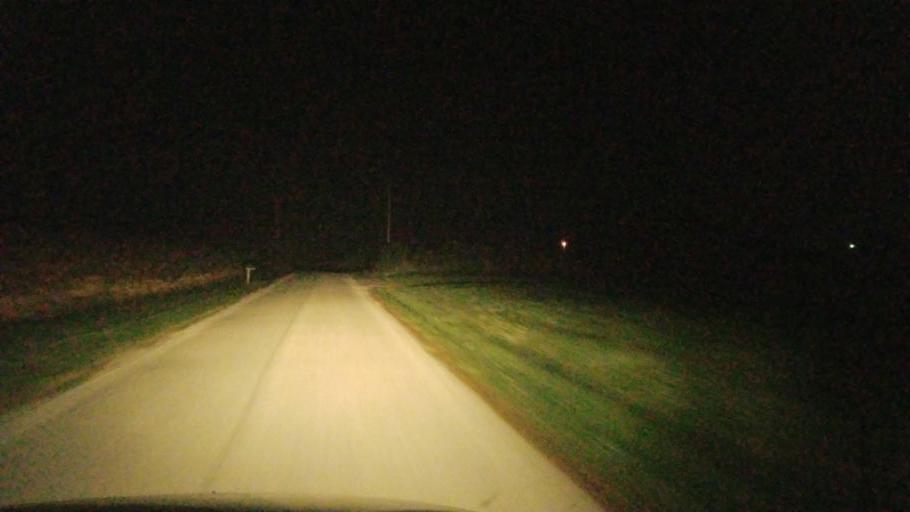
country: US
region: Ohio
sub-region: Highland County
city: Leesburg
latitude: 39.3021
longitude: -83.5620
